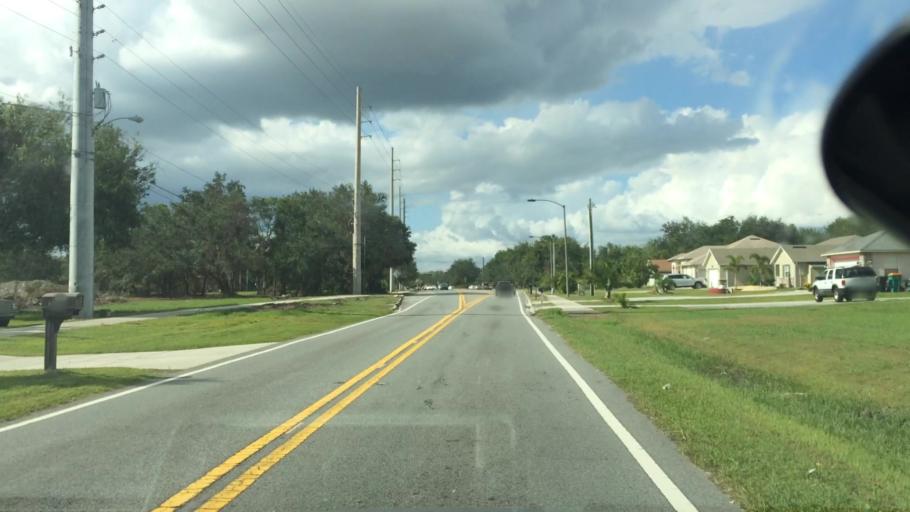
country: US
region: Florida
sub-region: Osceola County
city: Buenaventura Lakes
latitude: 28.2764
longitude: -81.3603
